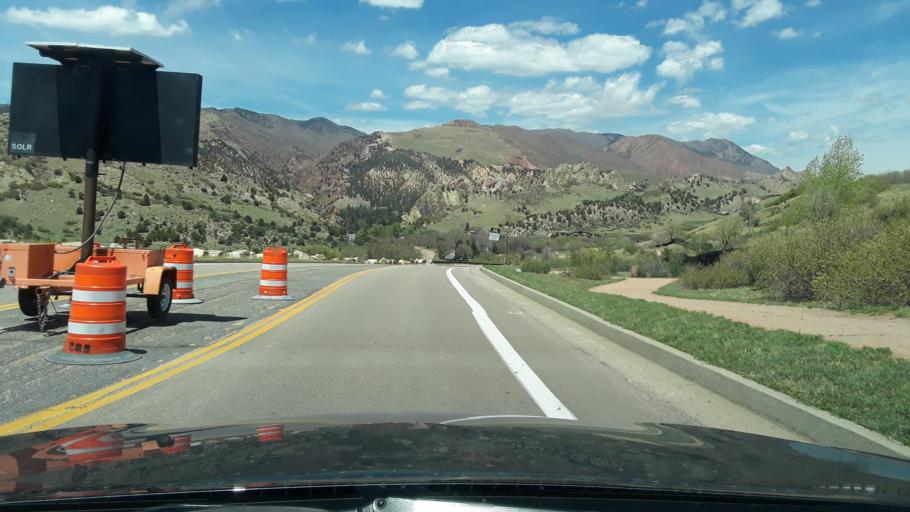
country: US
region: Colorado
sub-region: El Paso County
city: Manitou Springs
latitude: 38.8838
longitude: -104.8725
